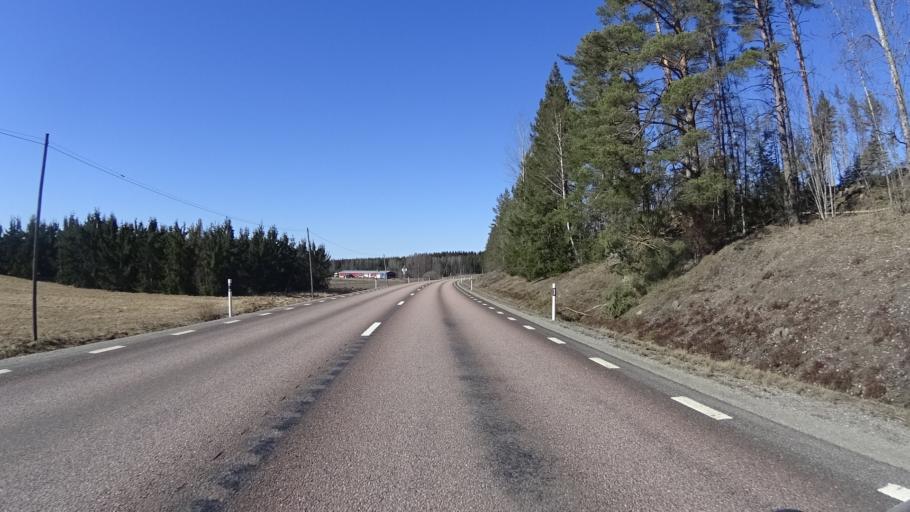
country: SE
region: Vaermland
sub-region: Sunne Kommun
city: Sunne
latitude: 59.6315
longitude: 12.9494
